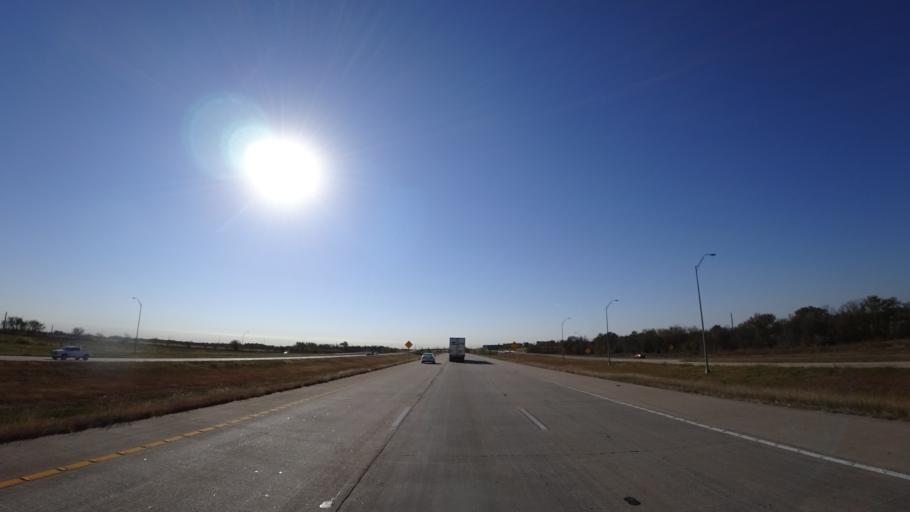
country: US
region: Texas
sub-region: Travis County
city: Pflugerville
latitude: 30.4333
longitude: -97.5908
